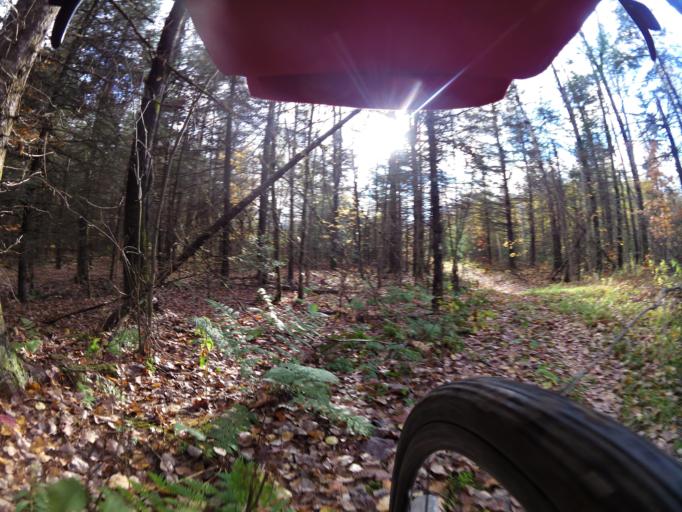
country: CA
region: Quebec
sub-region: Outaouais
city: Wakefield
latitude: 45.6704
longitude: -76.1266
